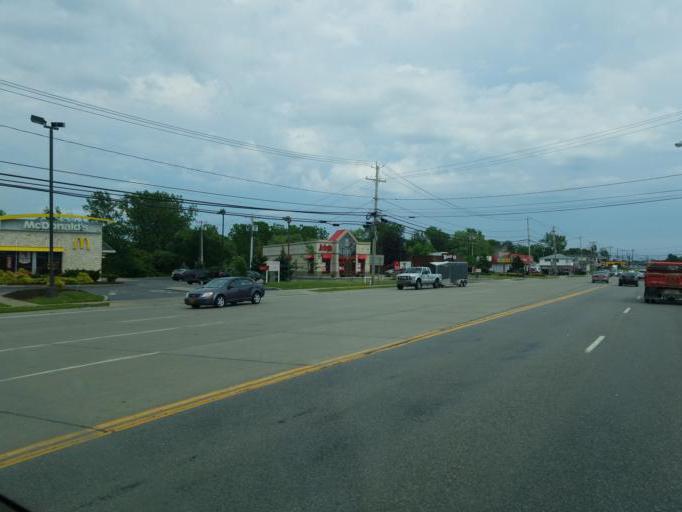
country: US
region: New York
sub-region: Erie County
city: Hamburg
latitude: 42.7491
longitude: -78.8542
